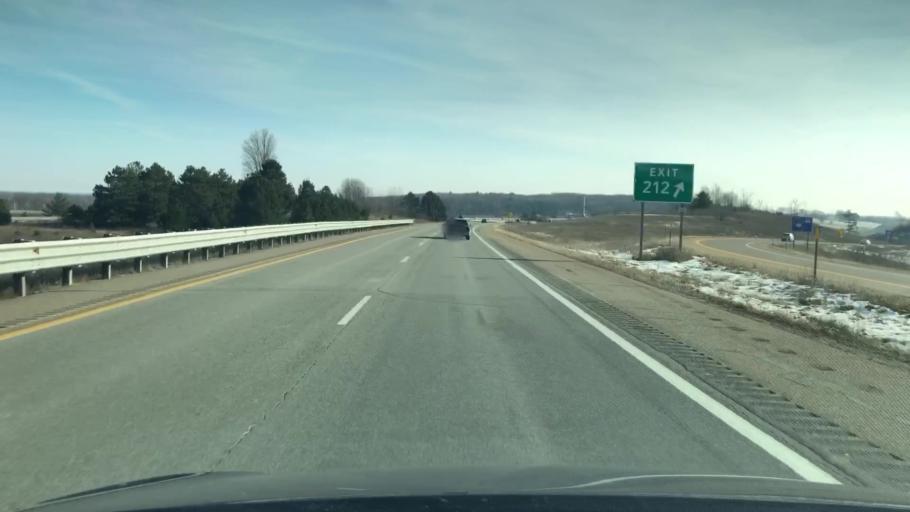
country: US
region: Michigan
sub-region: Ogemaw County
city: West Branch
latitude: 44.2458
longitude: -84.2297
